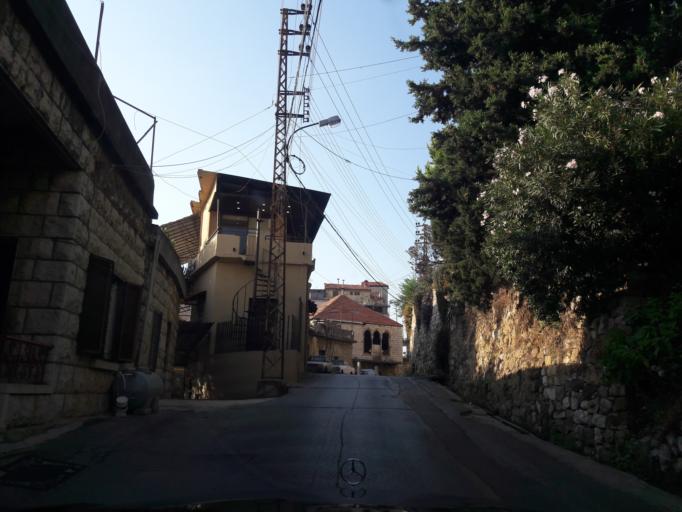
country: LB
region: Mont-Liban
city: Djounie
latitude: 33.9265
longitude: 35.6726
